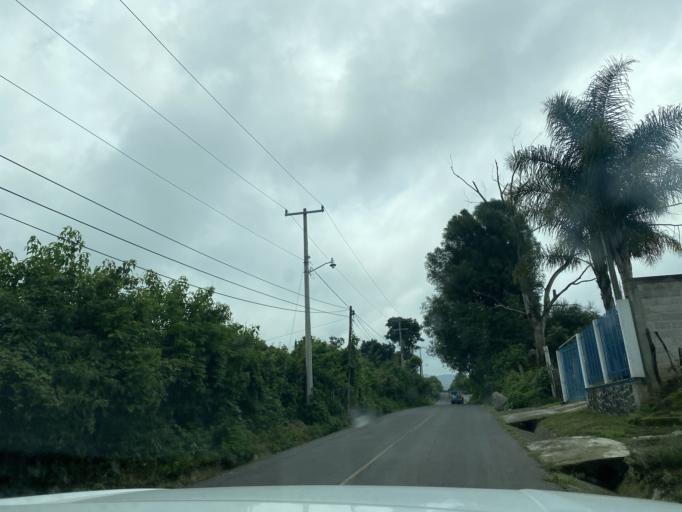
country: MX
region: Morelos
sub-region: Yecapixtla
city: Texcala
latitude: 18.9330
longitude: -98.8034
